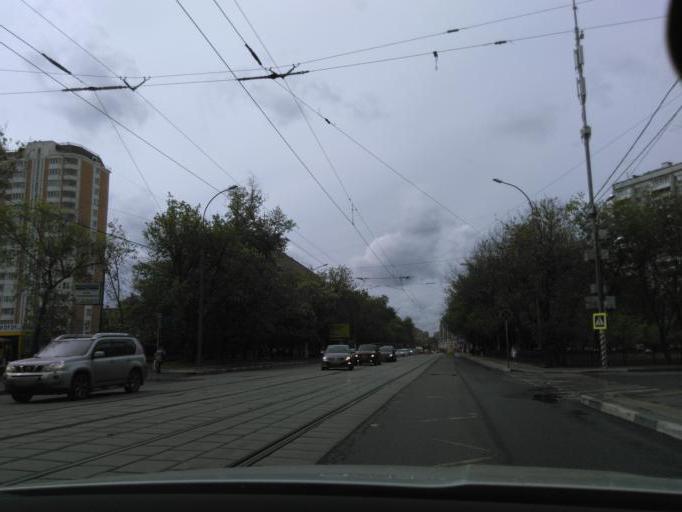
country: RU
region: Moscow
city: Taganskiy
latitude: 55.7429
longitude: 37.6765
